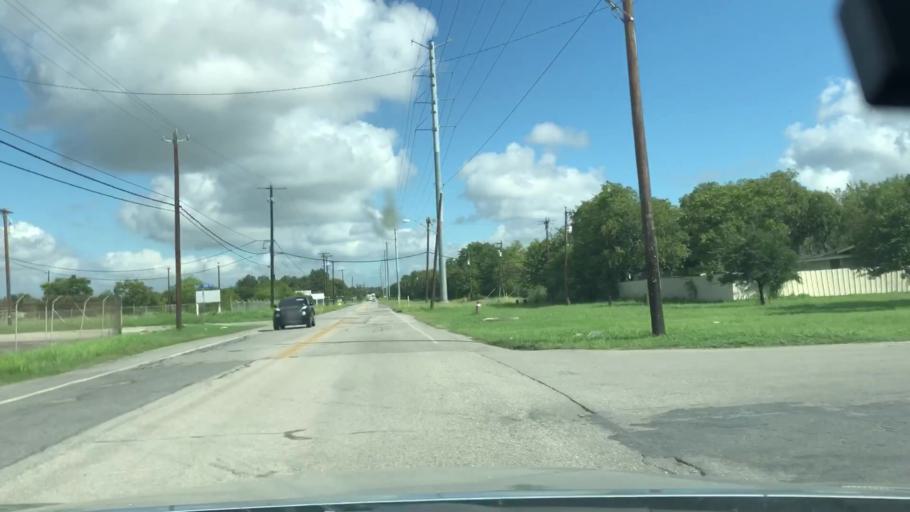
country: US
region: Texas
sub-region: Bexar County
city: Kirby
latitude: 29.4874
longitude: -98.3927
